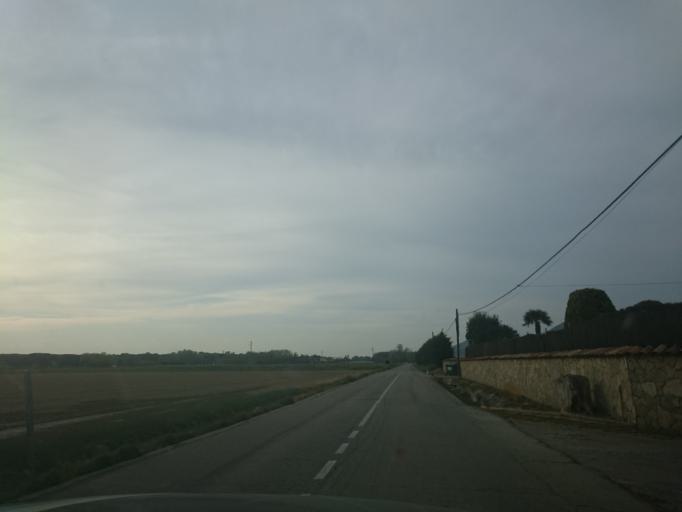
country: ES
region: Catalonia
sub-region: Provincia de Girona
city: Torroella de Montgri
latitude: 42.0164
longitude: 3.1478
